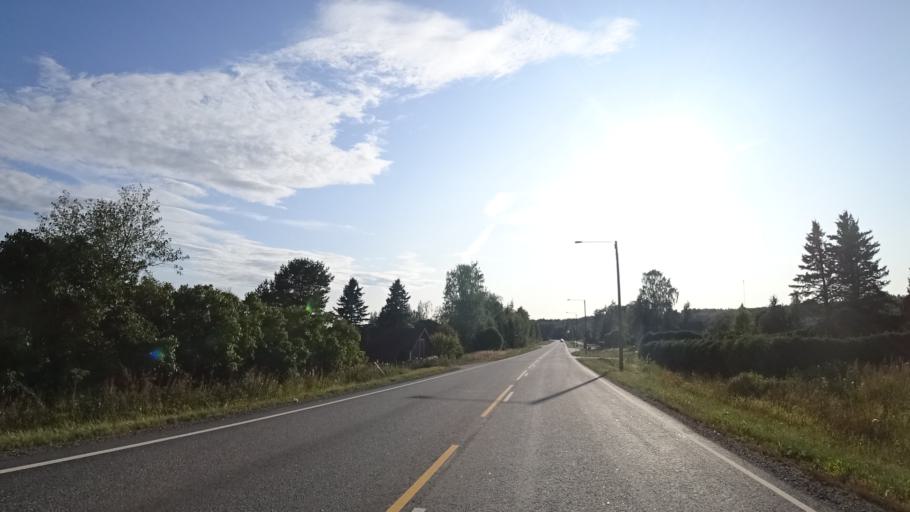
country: FI
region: South Karelia
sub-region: Imatra
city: Parikkala
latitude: 61.6090
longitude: 29.5053
